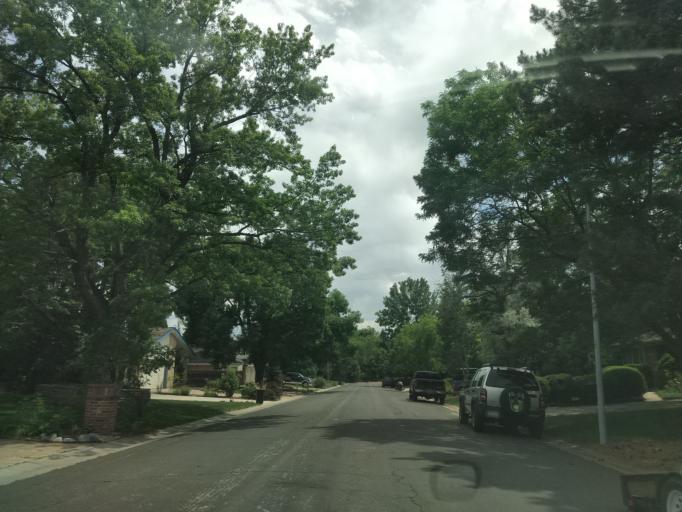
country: US
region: Colorado
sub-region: Jefferson County
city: Lakewood
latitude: 39.6866
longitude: -105.1279
